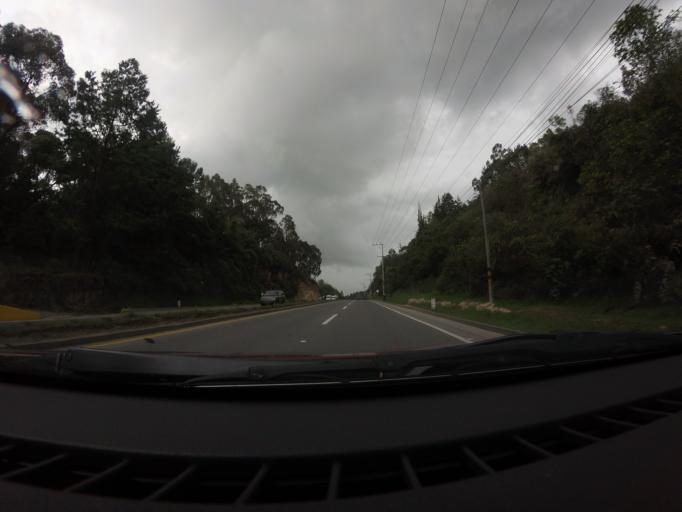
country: CO
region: Cundinamarca
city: El Rosal
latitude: 4.8033
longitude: -74.2105
